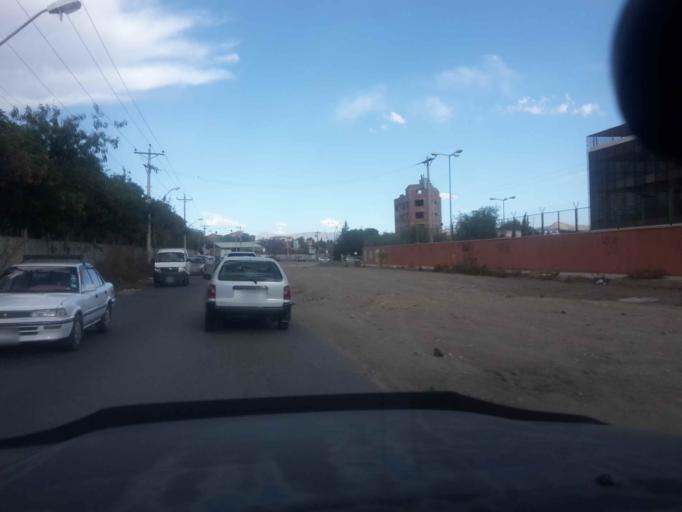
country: BO
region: Cochabamba
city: Cochabamba
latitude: -17.3496
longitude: -66.1862
